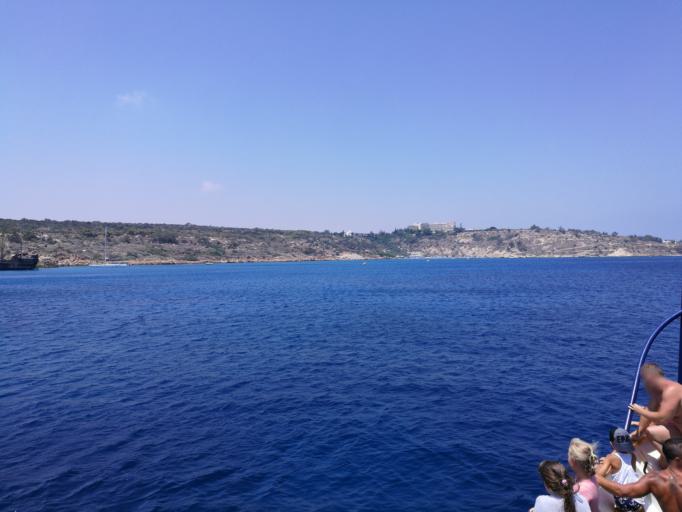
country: CY
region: Ammochostos
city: Protaras
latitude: 34.9774
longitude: 34.0763
